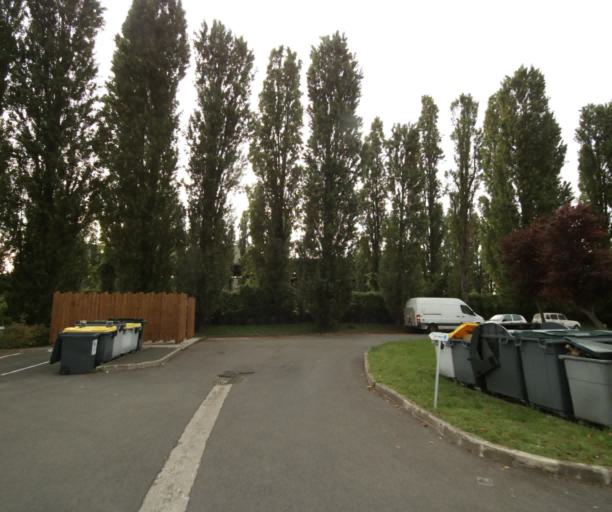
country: FR
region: Ile-de-France
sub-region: Departement des Hauts-de-Seine
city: Villeneuve-la-Garenne
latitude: 48.9230
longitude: 2.3193
